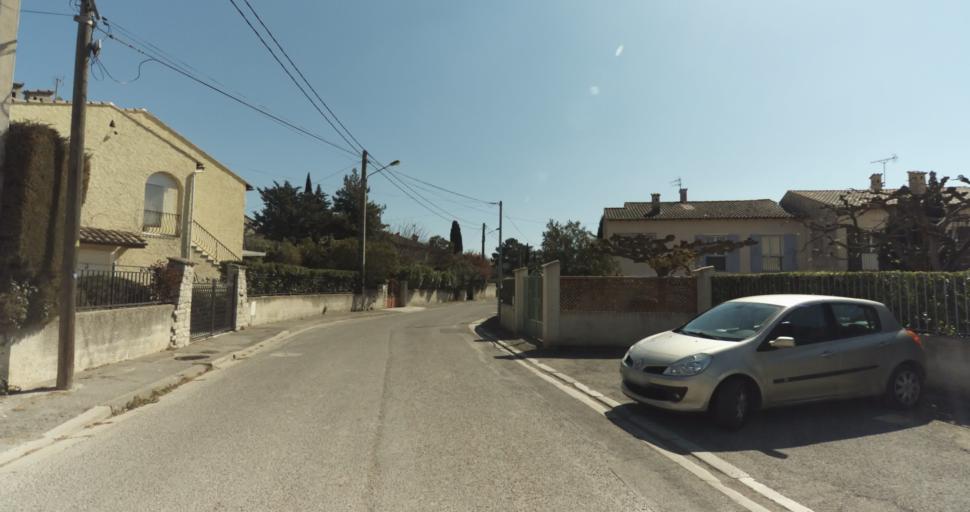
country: FR
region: Provence-Alpes-Cote d'Azur
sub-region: Departement des Bouches-du-Rhone
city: Pelissanne
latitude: 43.6320
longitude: 5.1622
